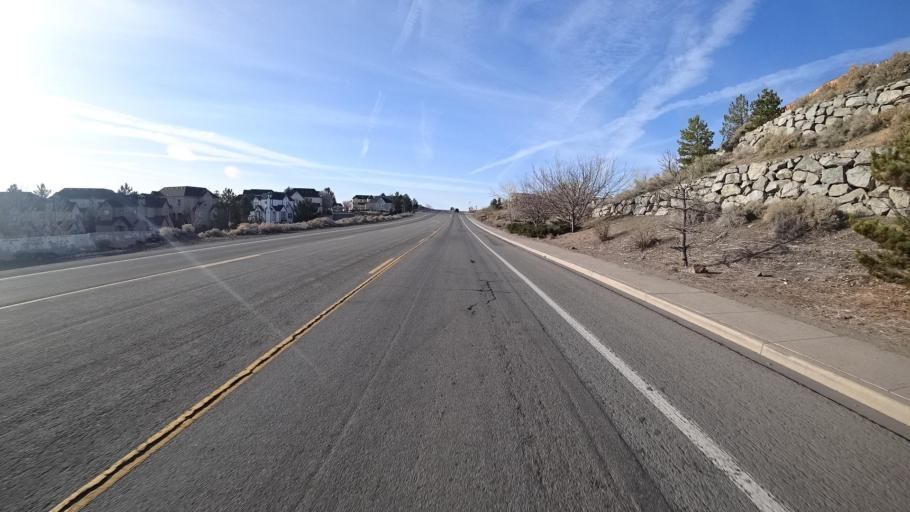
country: US
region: Nevada
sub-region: Washoe County
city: Sun Valley
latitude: 39.5630
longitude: -119.7738
